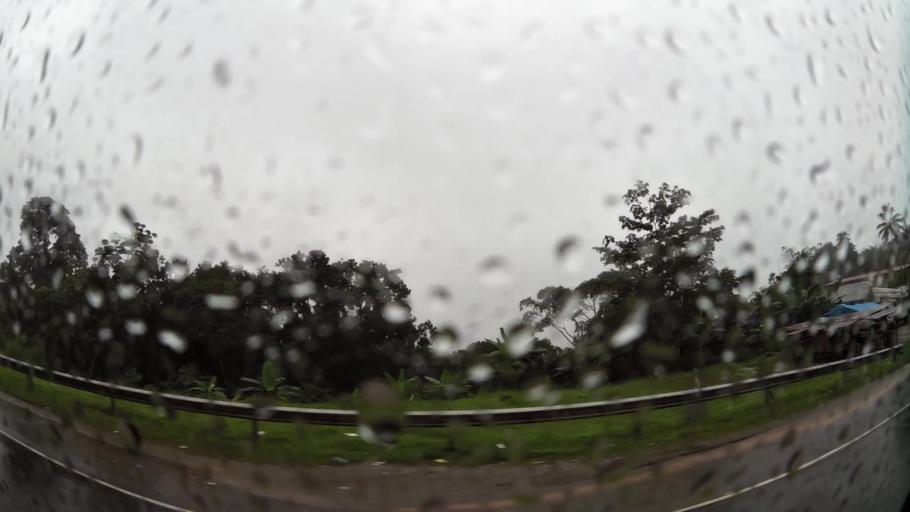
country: PA
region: Colon
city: Gatun
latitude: 9.2873
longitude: -79.7436
